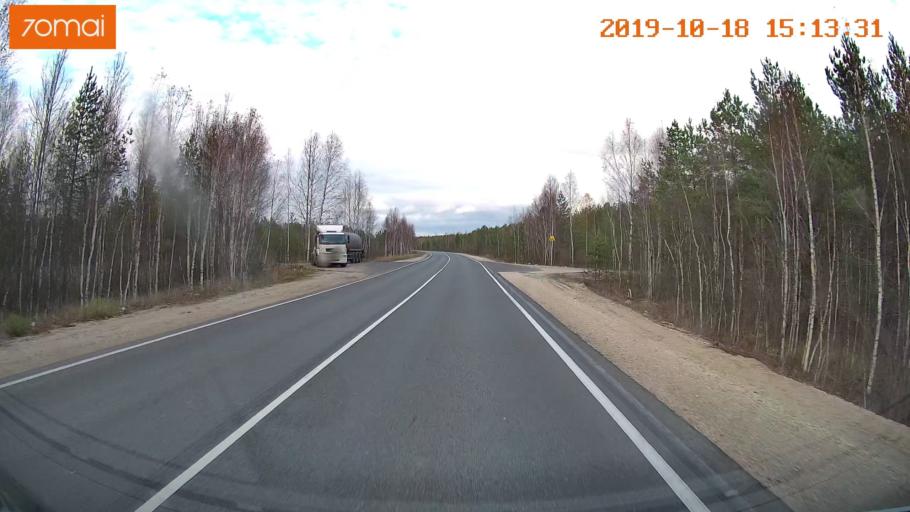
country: RU
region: Vladimir
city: Gus'-Khrustal'nyy
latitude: 55.5880
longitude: 40.7174
